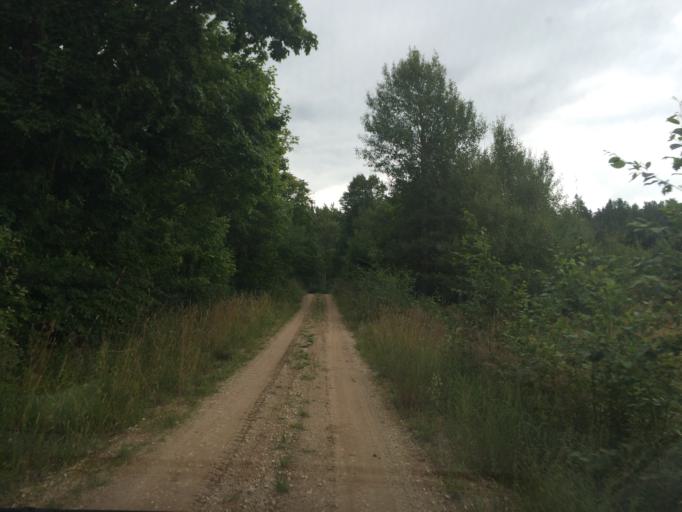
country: LV
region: Rezekne
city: Rezekne
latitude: 56.5851
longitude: 27.4128
